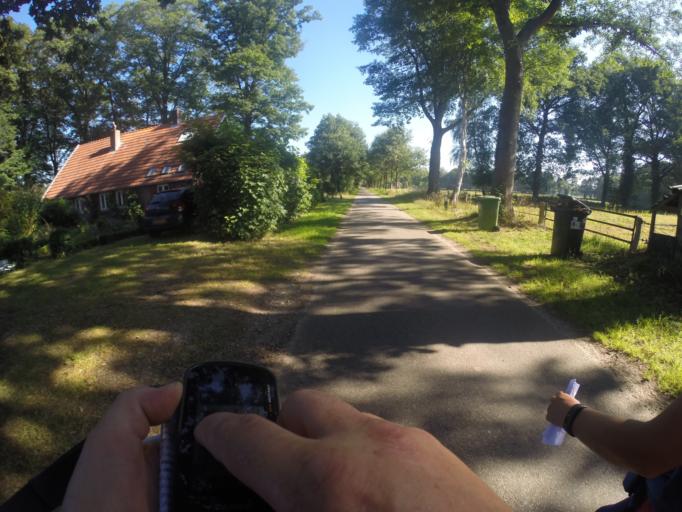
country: NL
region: Gelderland
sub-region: Gemeente Lochem
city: Almen
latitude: 52.1207
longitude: 6.3273
